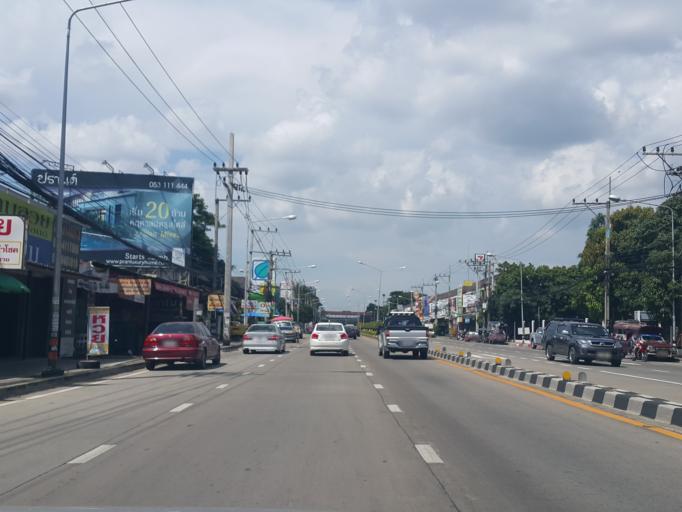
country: TH
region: Chiang Mai
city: Chiang Mai
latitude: 18.7758
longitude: 98.9766
